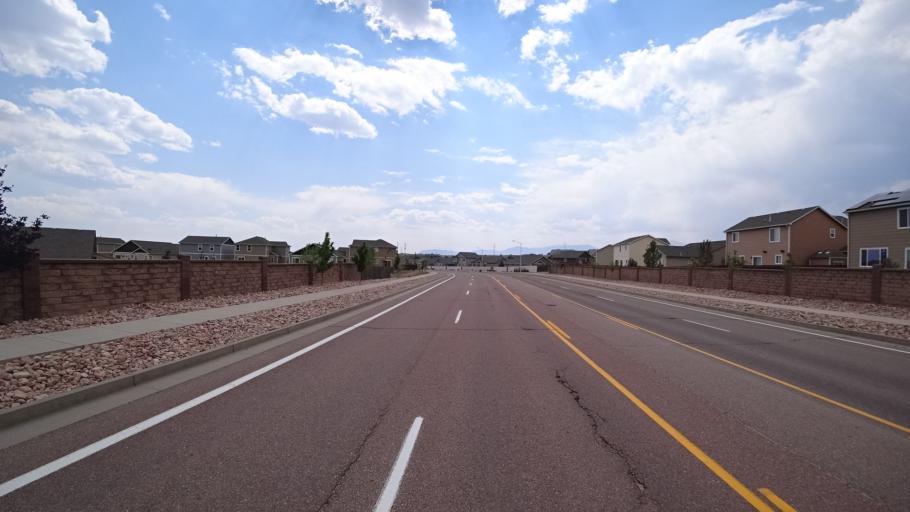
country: US
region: Colorado
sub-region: El Paso County
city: Black Forest
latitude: 38.9472
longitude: -104.6964
